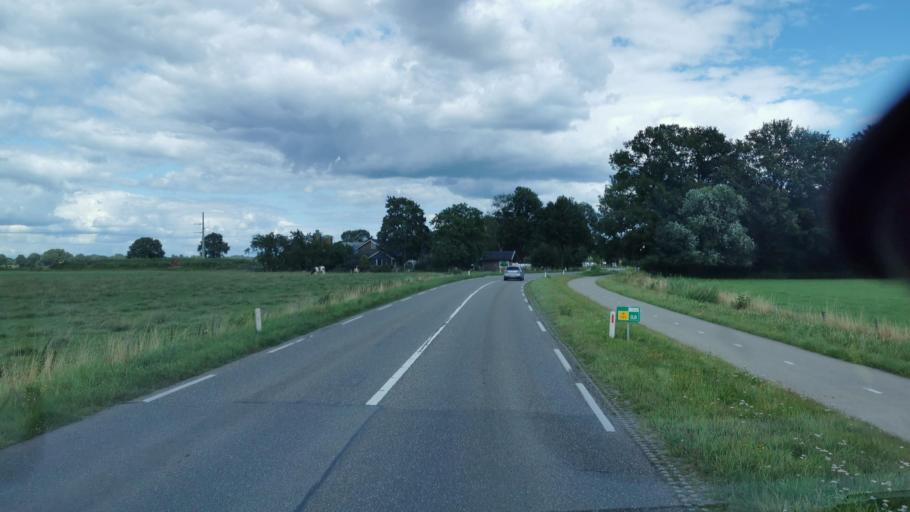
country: NL
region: Overijssel
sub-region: Gemeente Losser
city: Losser
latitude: 52.2262
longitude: 6.9804
